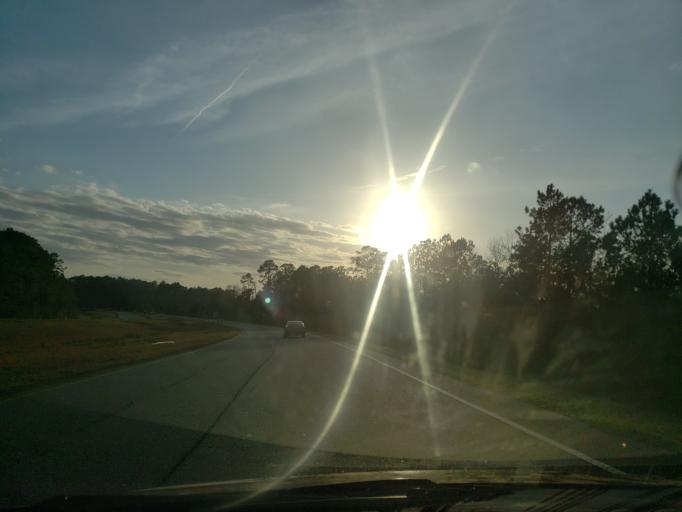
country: US
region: Georgia
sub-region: Chatham County
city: Bloomingdale
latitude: 32.1457
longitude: -81.3057
